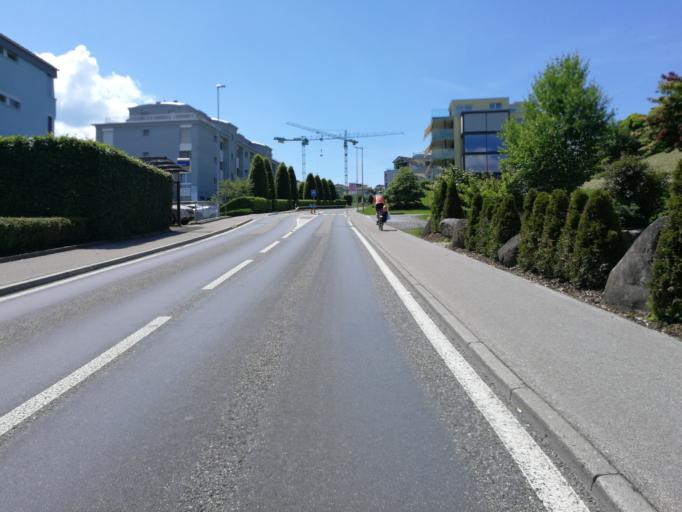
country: CH
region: Schwyz
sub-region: Bezirk Hoefe
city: Feusisberg
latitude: 47.1976
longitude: 8.7392
